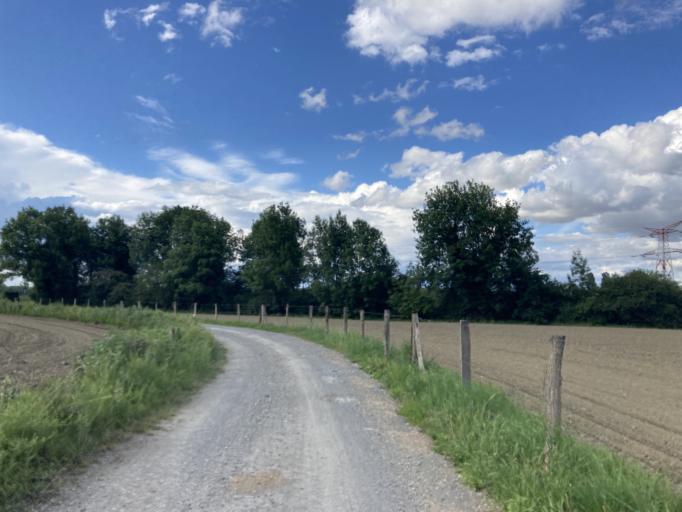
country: FR
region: Aquitaine
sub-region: Departement des Pyrenees-Atlantiques
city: Arbus
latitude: 43.3361
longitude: -0.5049
